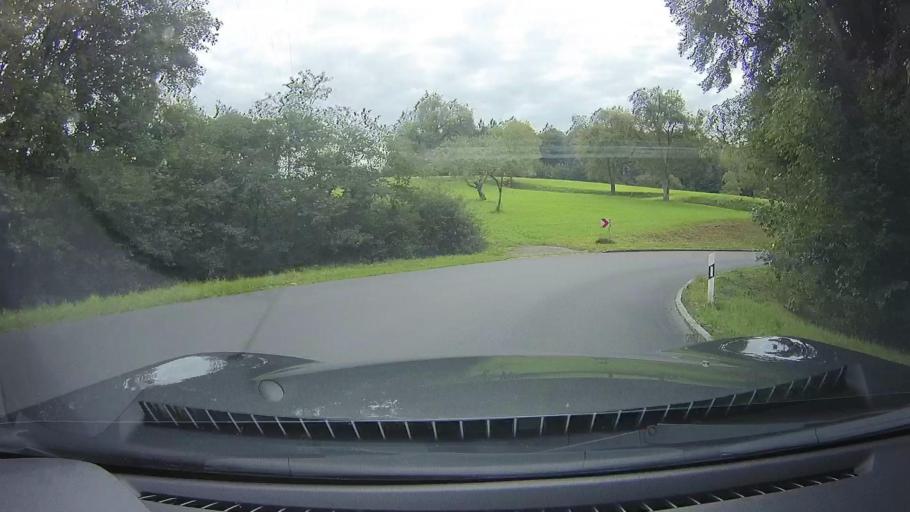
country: DE
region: Baden-Wuerttemberg
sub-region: Regierungsbezirk Stuttgart
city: Althutte
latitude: 48.9118
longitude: 9.5485
